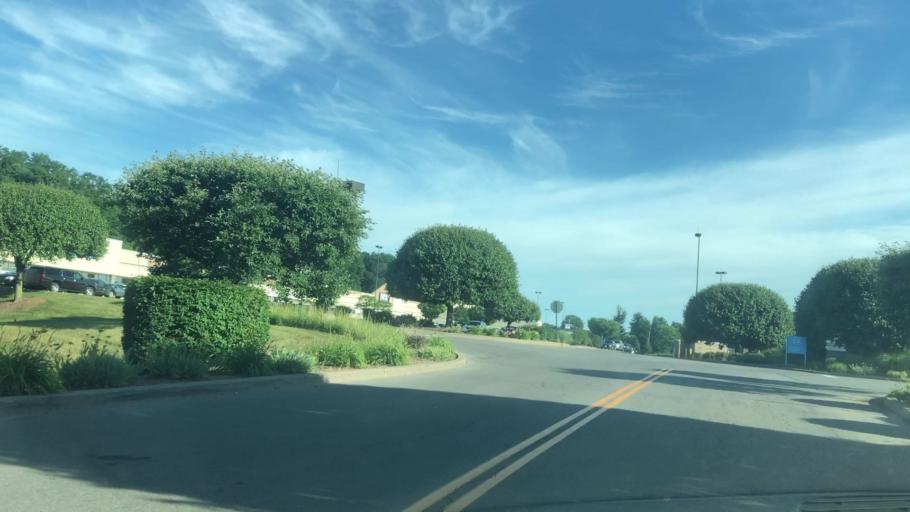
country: US
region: New York
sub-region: Ontario County
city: Victor
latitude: 43.0324
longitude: -77.4394
